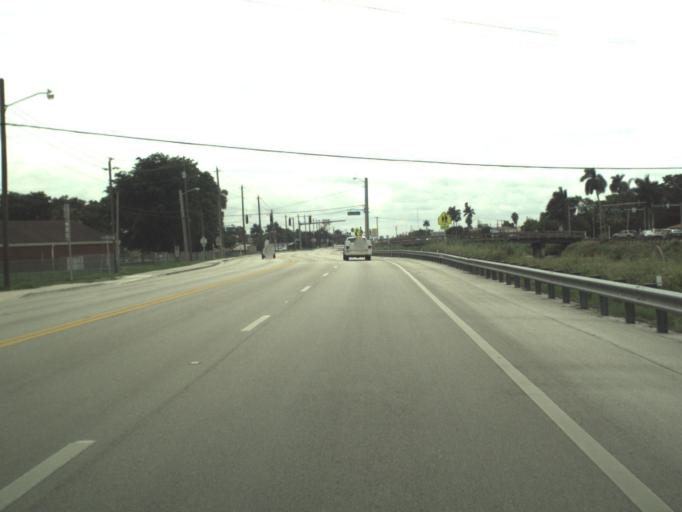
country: US
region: Florida
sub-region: Palm Beach County
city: Belle Glade
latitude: 26.6895
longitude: -80.6743
